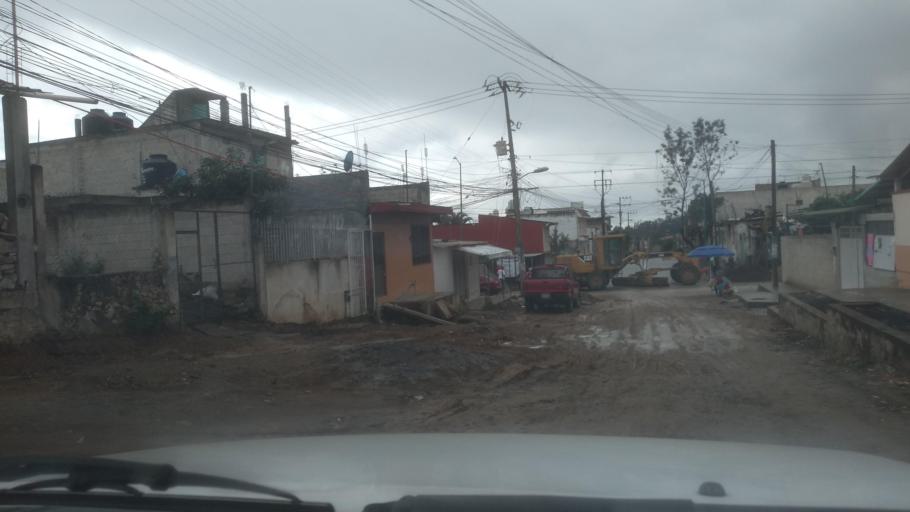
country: MX
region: Veracruz
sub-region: Emiliano Zapata
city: Las Trancas
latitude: 19.5051
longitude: -96.8692
